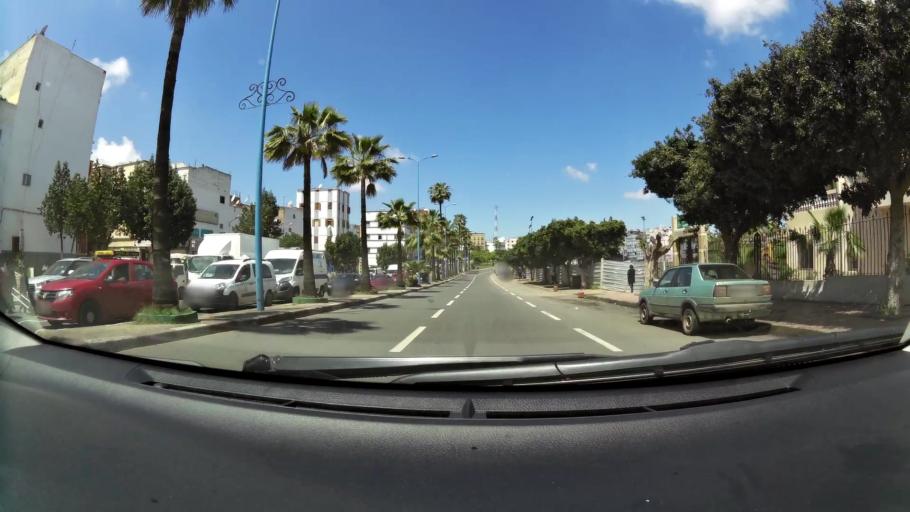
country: MA
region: Grand Casablanca
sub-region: Casablanca
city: Casablanca
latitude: 33.5538
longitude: -7.5707
